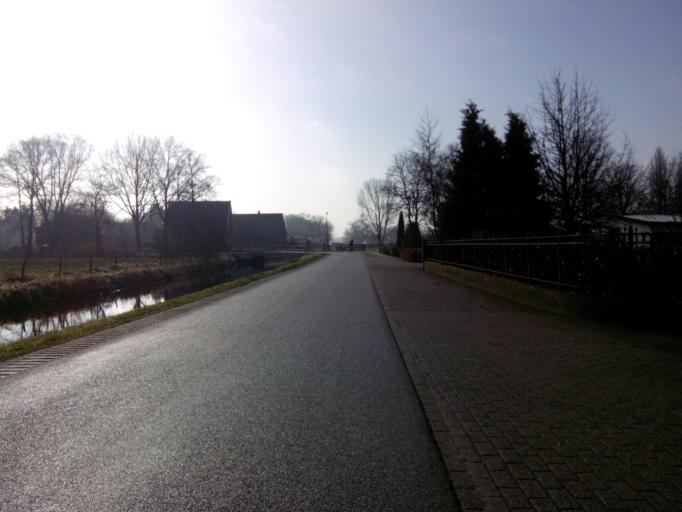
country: NL
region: Utrecht
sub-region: Gemeente Woudenberg
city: Woudenberg
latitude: 52.0718
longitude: 5.4074
